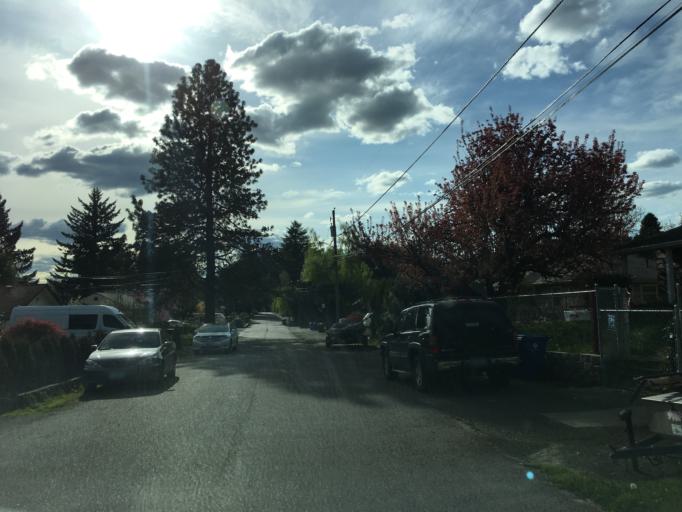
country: US
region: Oregon
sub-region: Multnomah County
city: Lents
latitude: 45.5403
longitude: -122.5535
